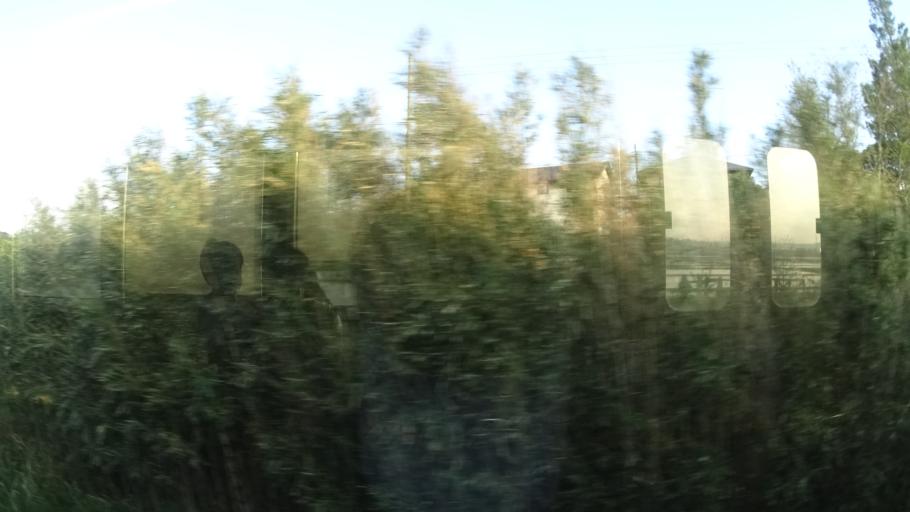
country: JP
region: Aichi
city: Tahara
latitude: 34.6776
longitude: 137.3189
